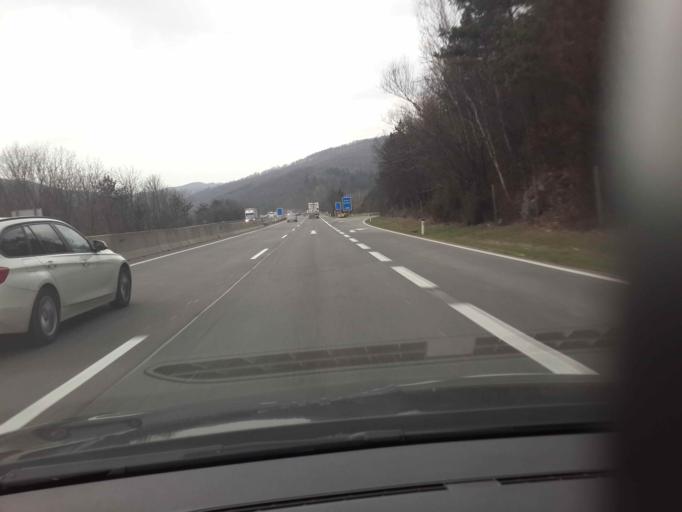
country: AT
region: Lower Austria
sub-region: Politischer Bezirk Baden
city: Alland
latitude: 48.0656
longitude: 16.0685
